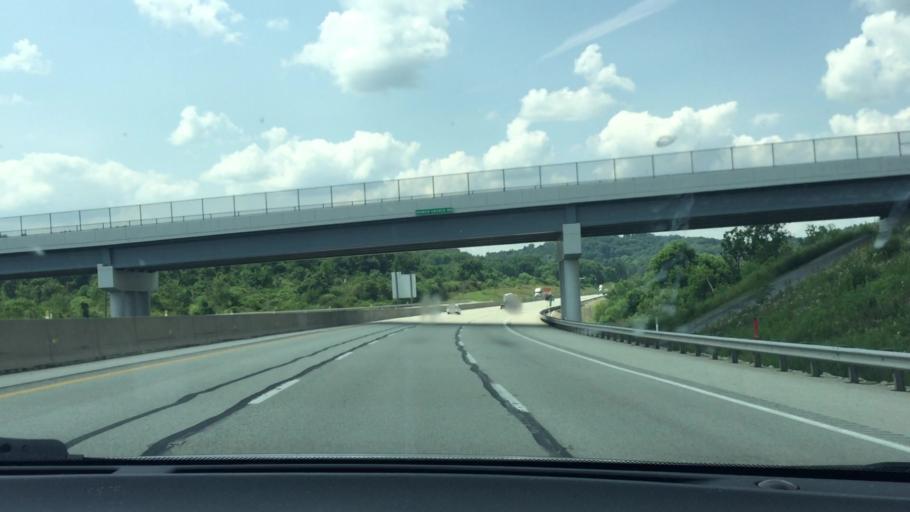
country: US
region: Pennsylvania
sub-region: Westmoreland County
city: New Stanton
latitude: 40.2426
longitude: -79.6355
